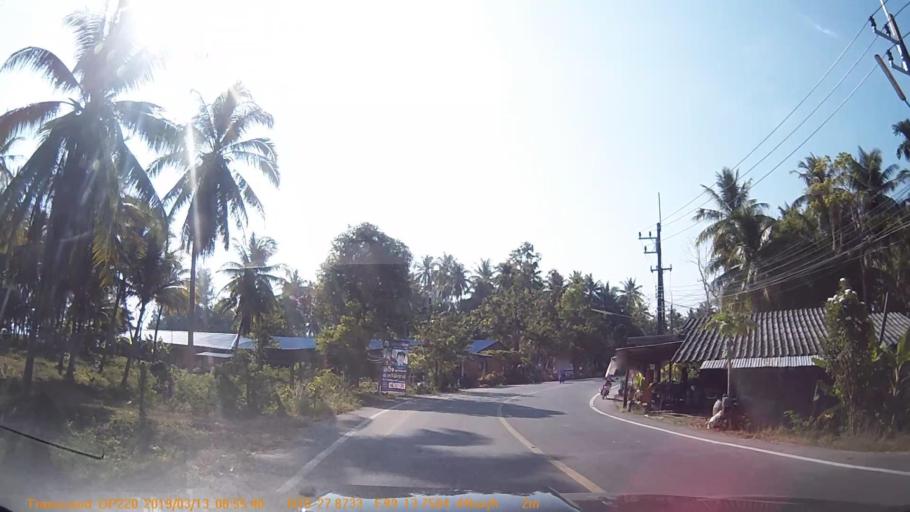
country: TH
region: Chumphon
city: Chumphon
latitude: 10.4645
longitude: 99.2294
